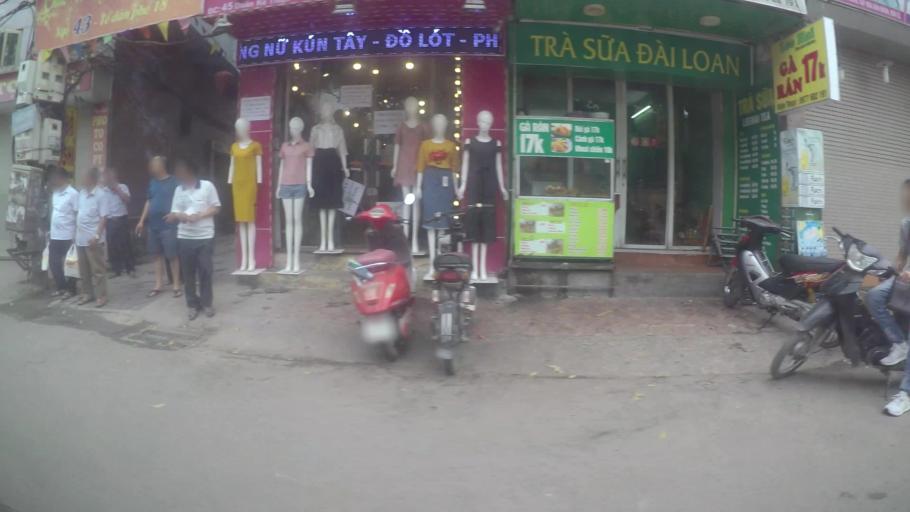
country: VN
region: Ha Noi
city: Cau Dien
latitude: 21.0410
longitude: 105.7790
